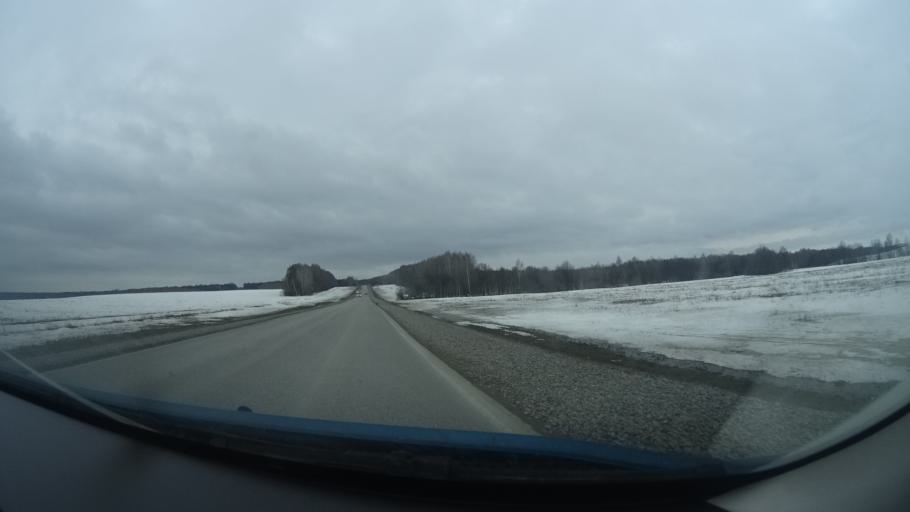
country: RU
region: Bashkortostan
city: Birsk
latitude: 55.3469
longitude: 55.5888
